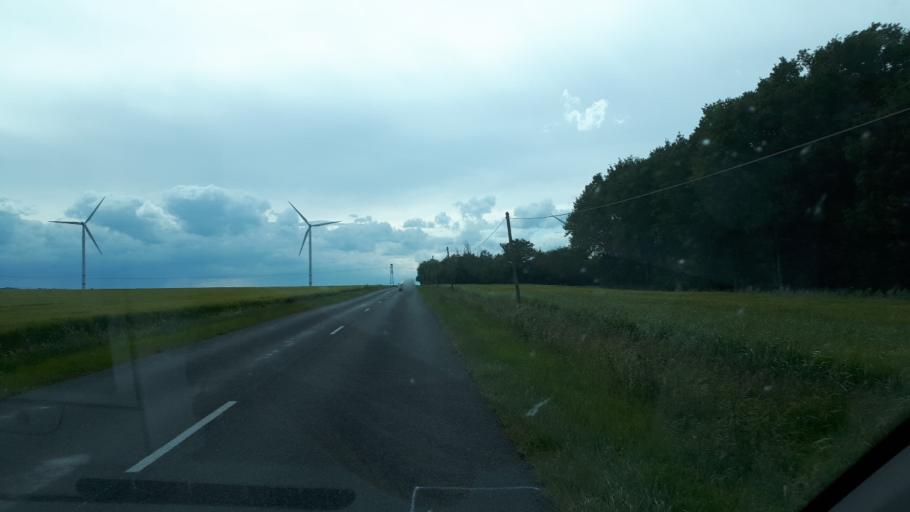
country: FR
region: Centre
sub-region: Departement du Cher
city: Marmagne
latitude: 47.0810
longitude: 2.2503
